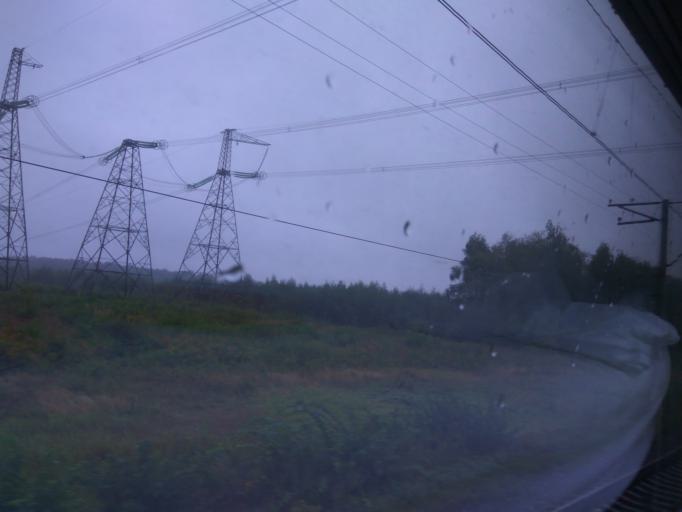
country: RU
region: Moskovskaya
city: Ozherel'ye
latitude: 54.7542
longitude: 38.3380
